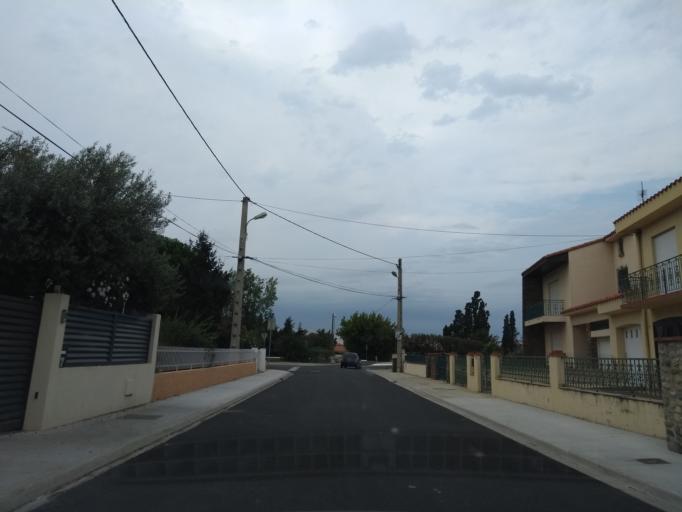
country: FR
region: Languedoc-Roussillon
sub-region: Departement des Pyrenees-Orientales
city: Elne
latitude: 42.6041
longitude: 2.9688
